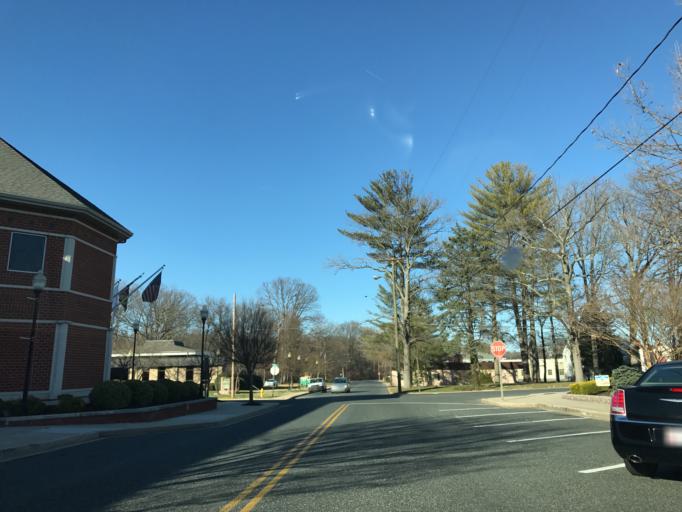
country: US
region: Maryland
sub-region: Harford County
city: Aberdeen
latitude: 39.5117
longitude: -76.1643
